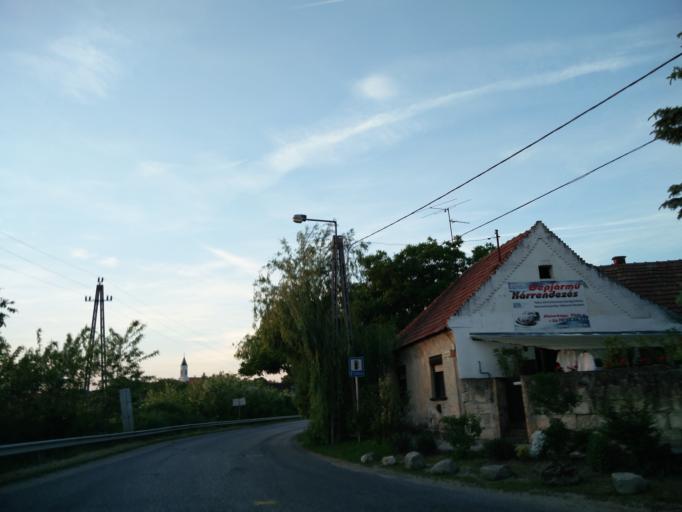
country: HU
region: Pest
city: Biatorbagy
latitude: 47.4589
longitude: 18.8109
